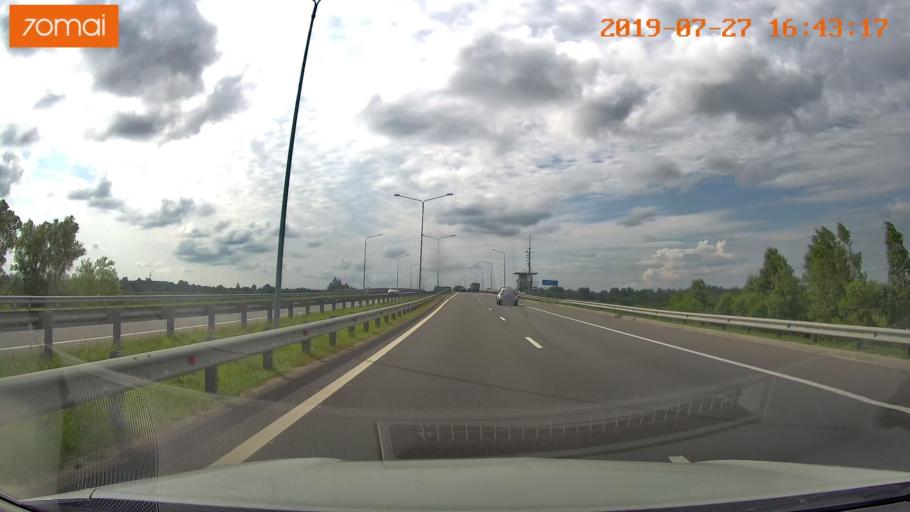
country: RU
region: Kaliningrad
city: Gvardeysk
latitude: 54.6703
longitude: 21.1072
